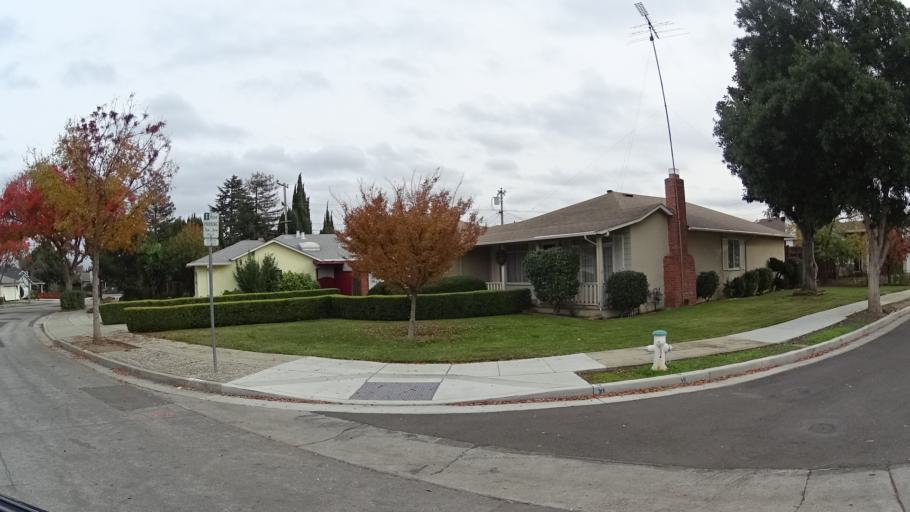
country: US
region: California
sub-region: Santa Clara County
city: Sunnyvale
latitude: 37.3706
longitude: -122.0502
